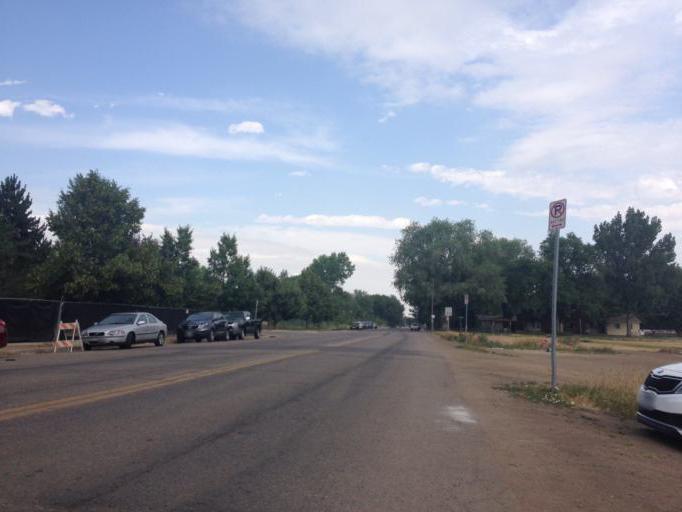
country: US
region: Colorado
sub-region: Larimer County
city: Fort Collins
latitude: 40.5924
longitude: -105.0687
